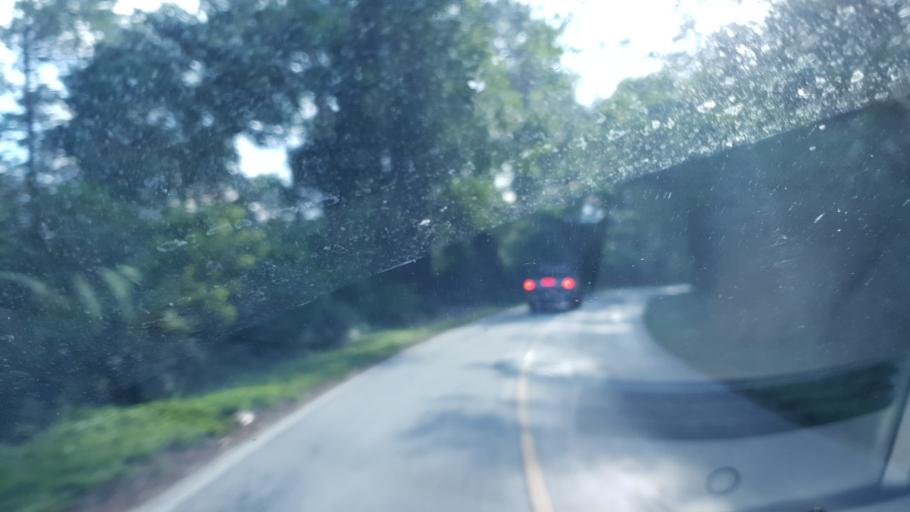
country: TH
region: Chiang Mai
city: Mae Chaem
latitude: 18.5112
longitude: 98.4767
